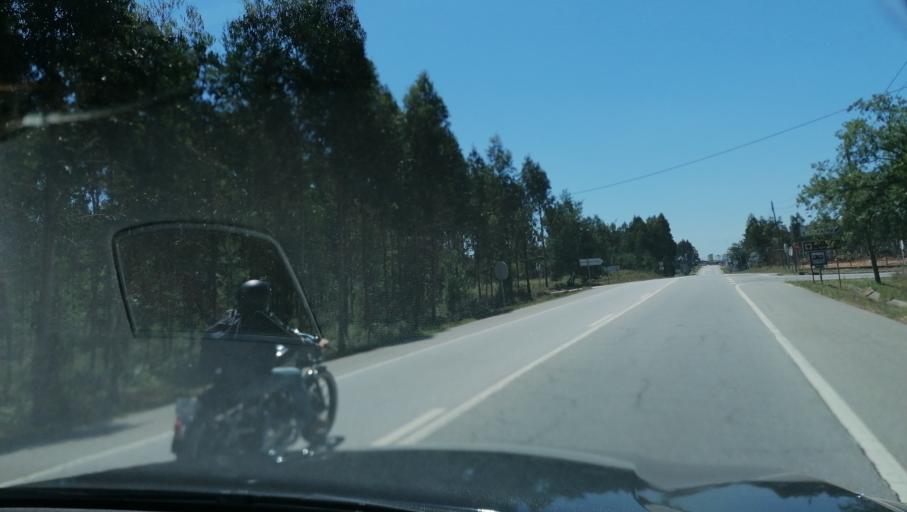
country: PT
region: Aveiro
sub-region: Anadia
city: Sangalhos
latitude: 40.4946
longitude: -8.4443
